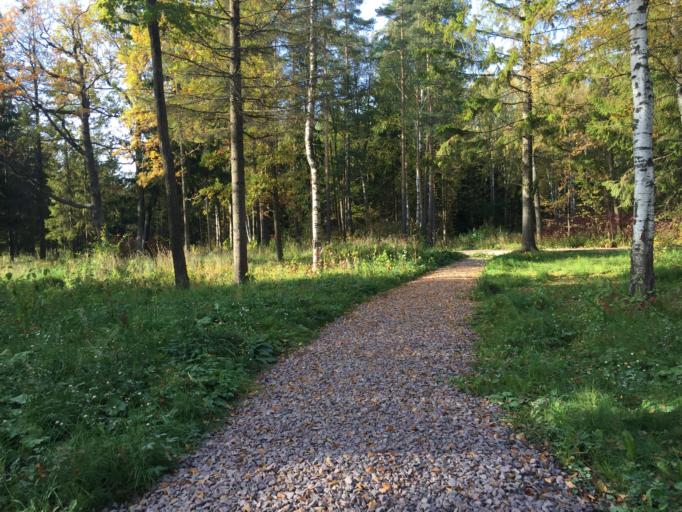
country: RU
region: St.-Petersburg
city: Pushkin
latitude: 59.7159
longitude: 30.3793
